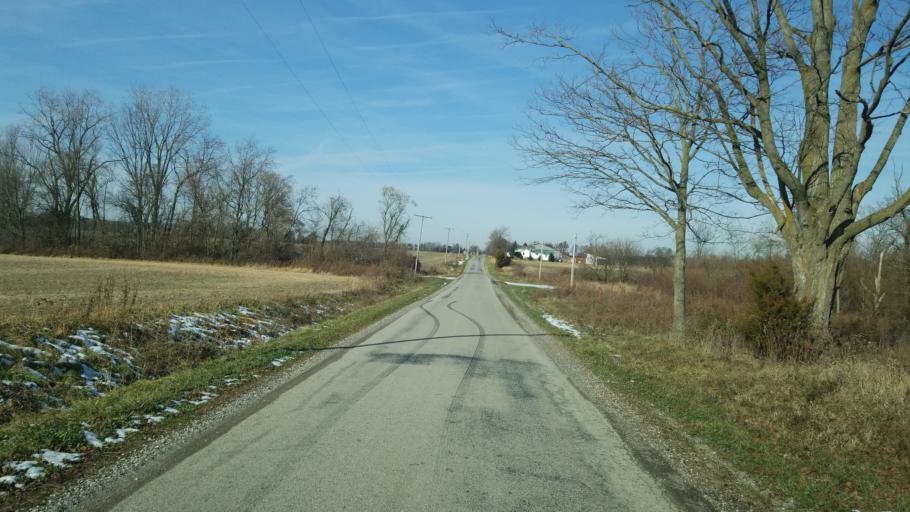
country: US
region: Ohio
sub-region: Huron County
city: Wakeman
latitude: 41.2264
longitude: -82.4173
